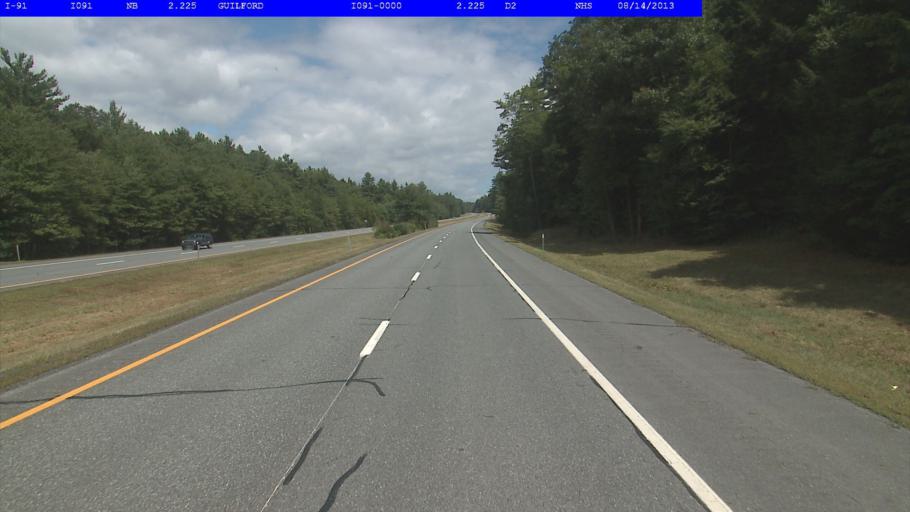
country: US
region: New Hampshire
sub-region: Cheshire County
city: Hinsdale
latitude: 42.7619
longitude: -72.5647
